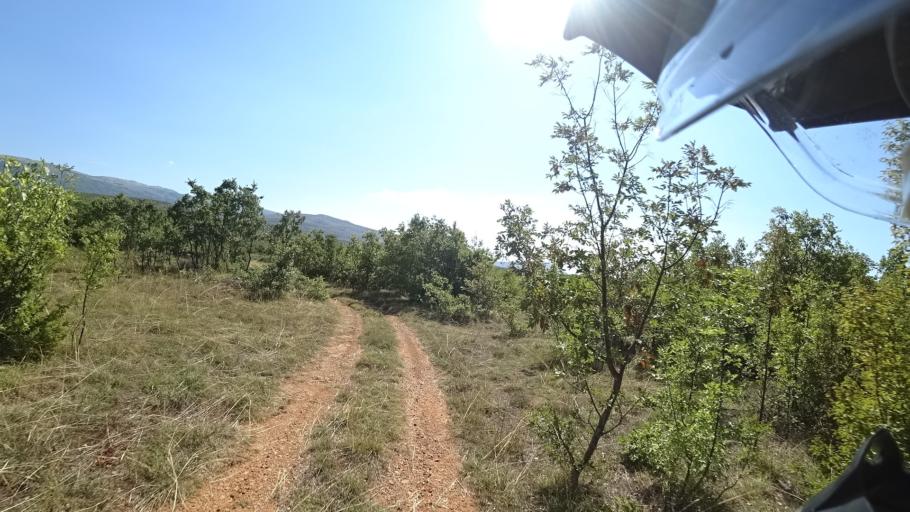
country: HR
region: Sibensko-Kniniska
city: Drnis
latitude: 43.8492
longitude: 16.2759
